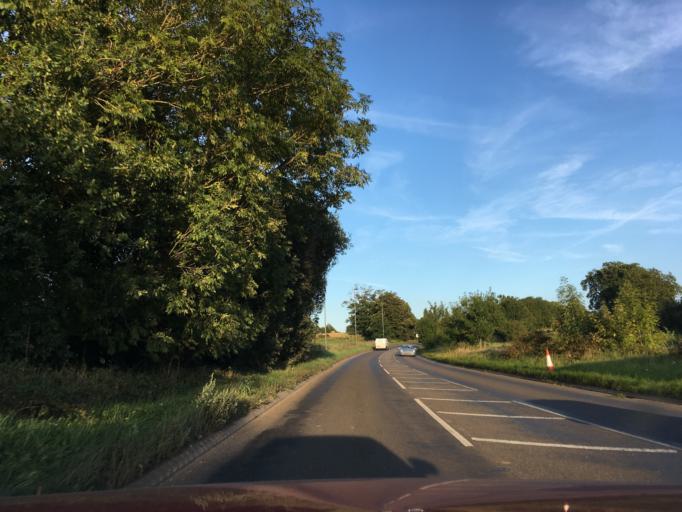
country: GB
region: England
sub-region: South Gloucestershire
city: Tytherington
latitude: 51.5526
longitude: -2.4650
